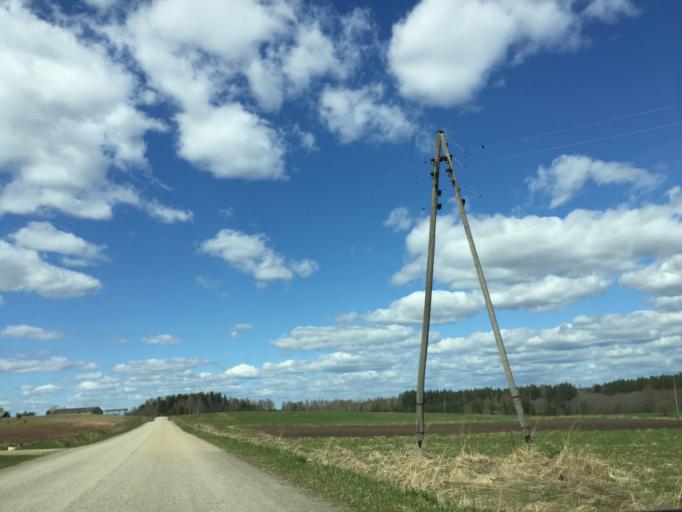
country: LV
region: Rezekne
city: Rezekne
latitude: 56.5699
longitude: 27.1373
